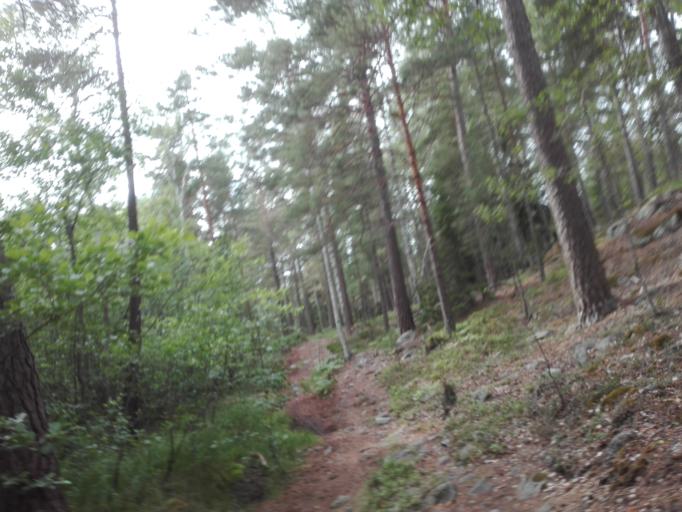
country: SE
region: Stockholm
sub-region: Nacka Kommun
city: Fisksatra
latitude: 59.2823
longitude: 18.2476
